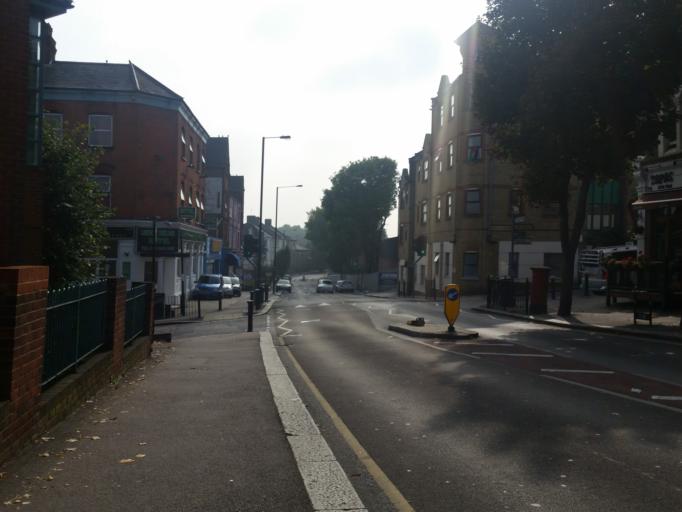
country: GB
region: England
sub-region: Greater London
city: Harringay
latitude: 51.5780
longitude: -0.1041
